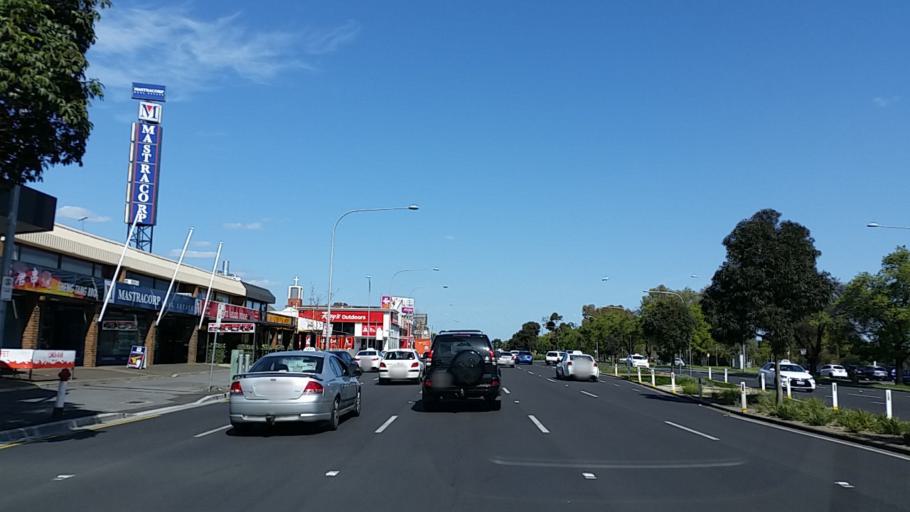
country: AU
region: South Australia
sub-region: Adelaide
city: Adelaide
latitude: -34.9255
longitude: 138.5877
